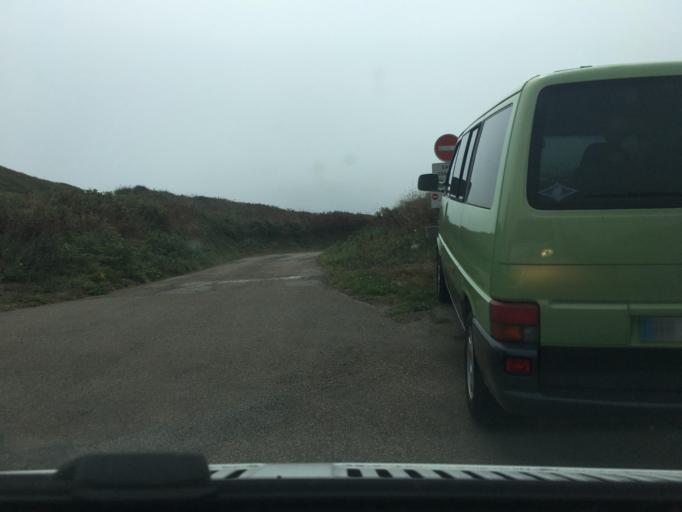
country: FR
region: Brittany
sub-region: Departement du Finistere
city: Plogoff
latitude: 48.0296
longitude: -4.6960
